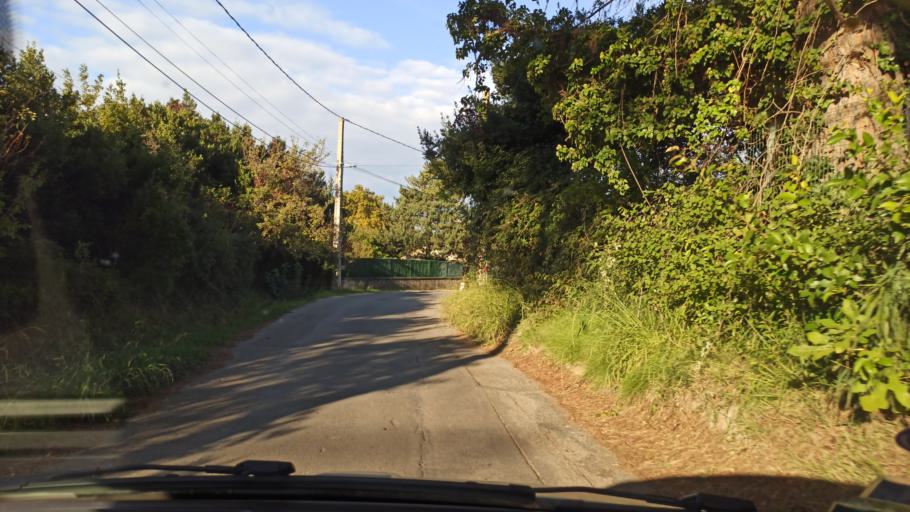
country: FR
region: Provence-Alpes-Cote d'Azur
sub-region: Departement du Vaucluse
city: Montfavet
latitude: 43.9330
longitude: 4.8854
